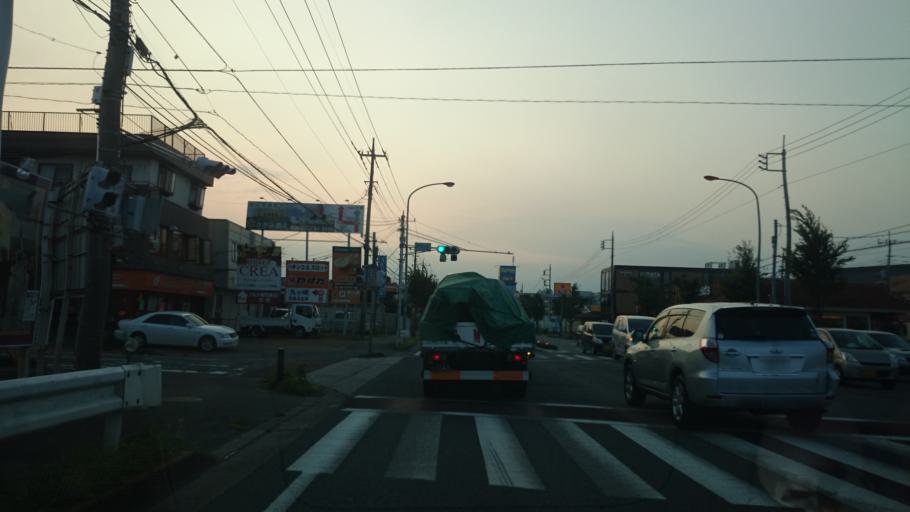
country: JP
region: Saitama
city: Hasuda
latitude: 35.9541
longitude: 139.6629
